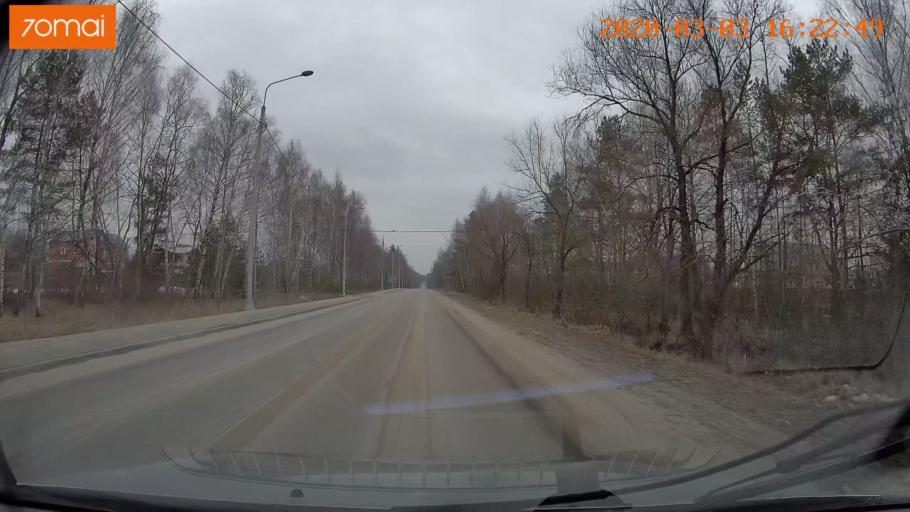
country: RU
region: Moskovskaya
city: Imeni Tsyurupy
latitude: 55.4897
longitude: 38.6491
